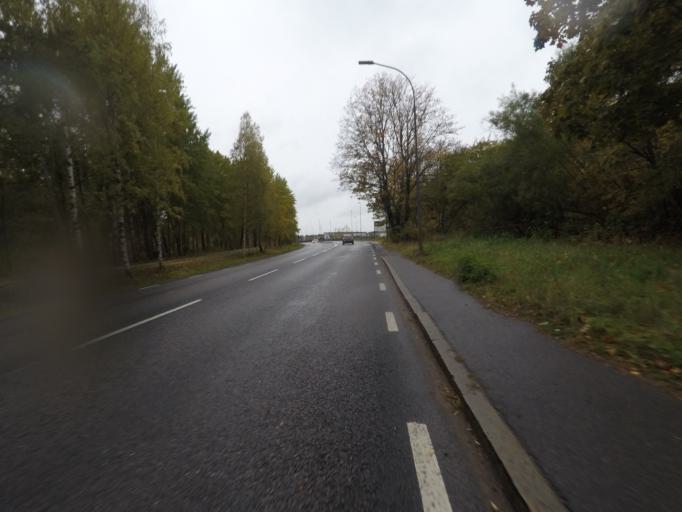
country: SE
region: OErebro
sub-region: Karlskoga Kommun
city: Karlskoga
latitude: 59.3213
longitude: 14.4763
